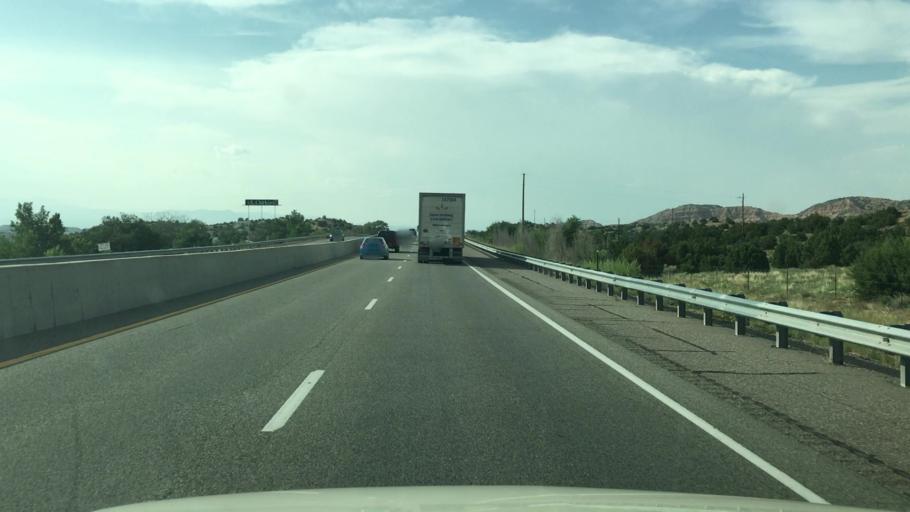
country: US
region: New Mexico
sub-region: Santa Fe County
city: Nambe
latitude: 35.8064
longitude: -105.9641
